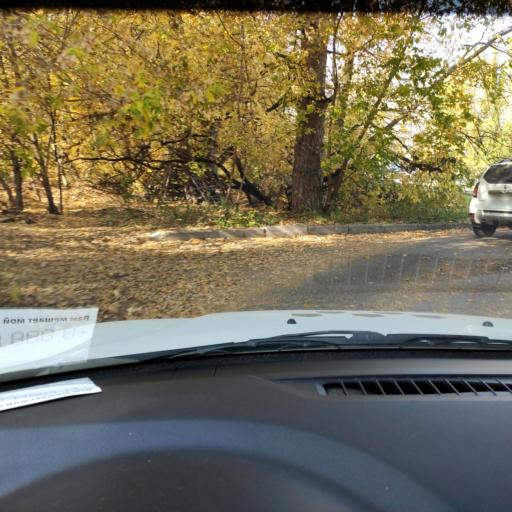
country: RU
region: Samara
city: Tol'yatti
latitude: 53.5074
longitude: 49.4494
